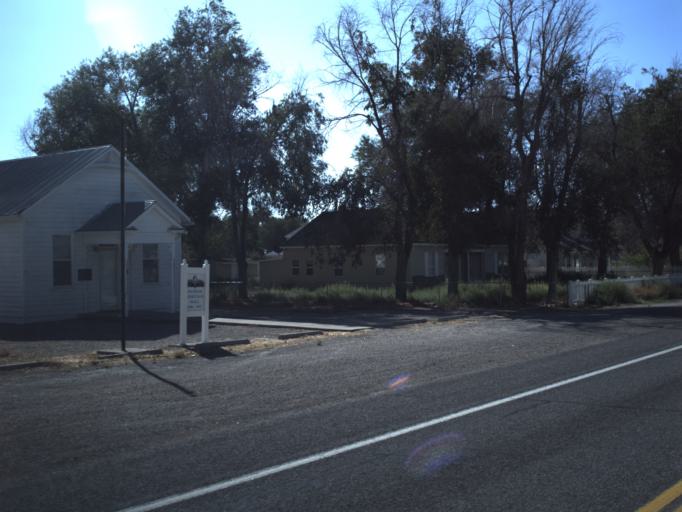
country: US
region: Utah
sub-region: Millard County
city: Delta
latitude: 39.2893
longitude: -112.6527
